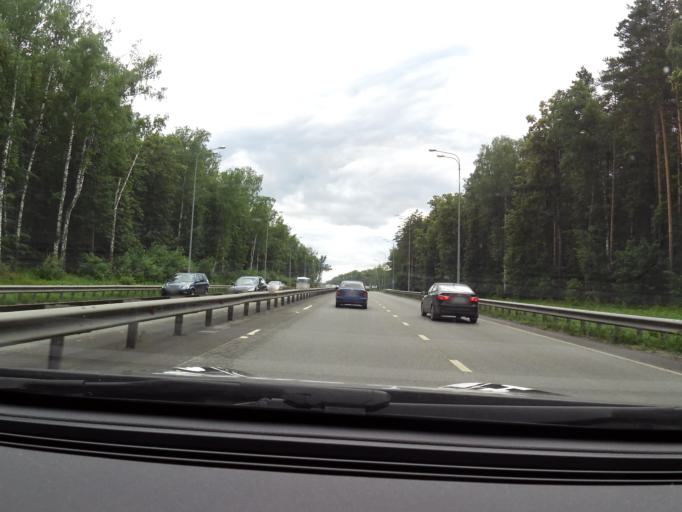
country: RU
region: Tatarstan
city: Staroye Arakchino
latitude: 55.8447
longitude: 48.9316
